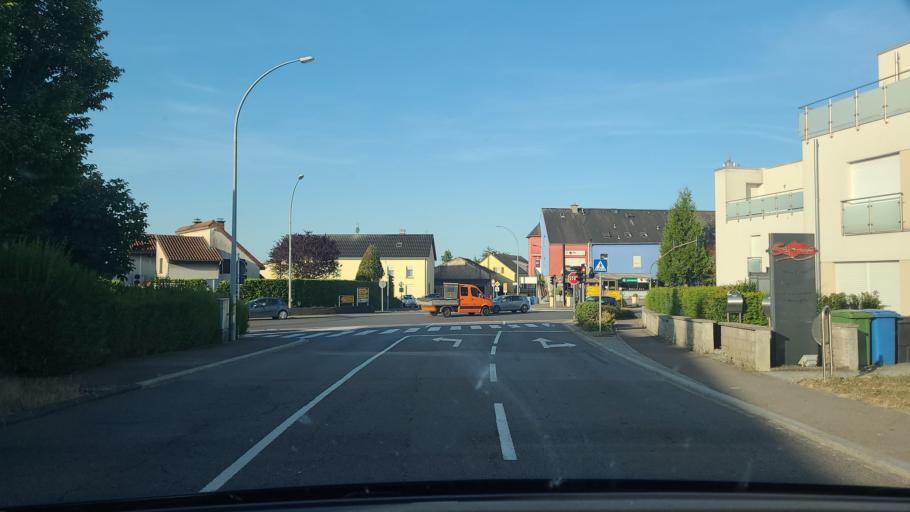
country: LU
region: Luxembourg
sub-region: Canton de Capellen
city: Dippach
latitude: 49.5876
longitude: 5.9857
